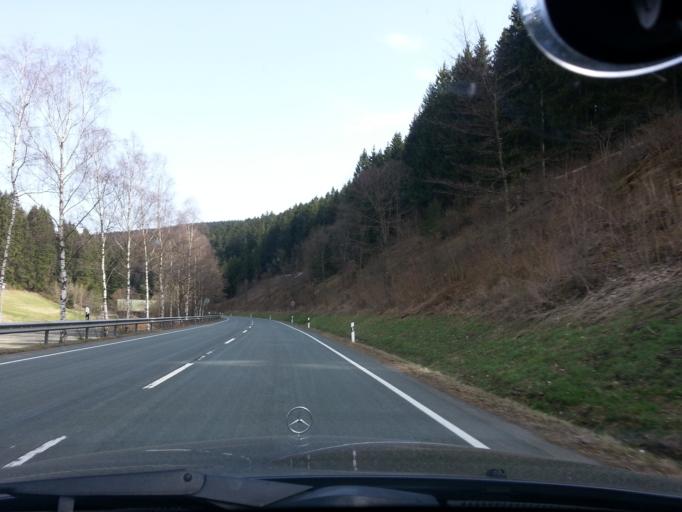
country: DE
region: North Rhine-Westphalia
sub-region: Regierungsbezirk Arnsberg
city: Bad Fredeburg
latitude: 51.2353
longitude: 8.3578
